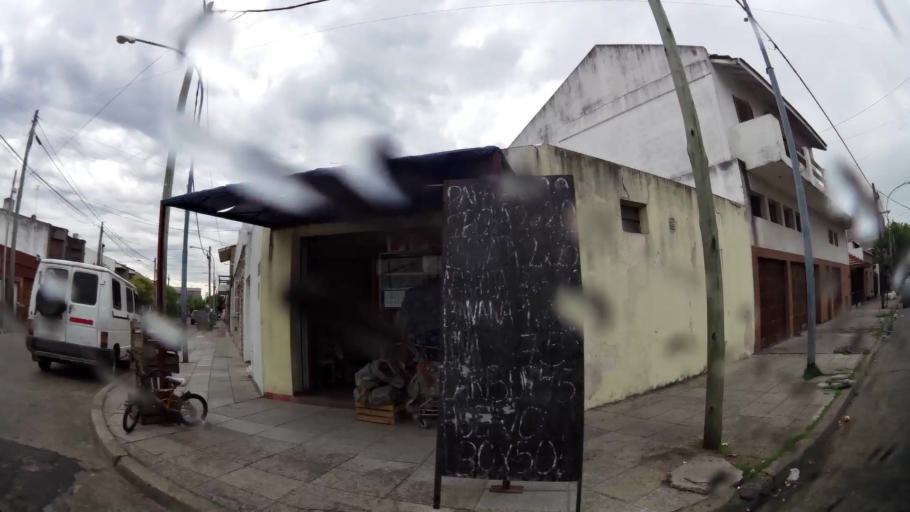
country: AR
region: Buenos Aires
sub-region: Partido de Lanus
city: Lanus
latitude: -34.6836
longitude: -58.4024
